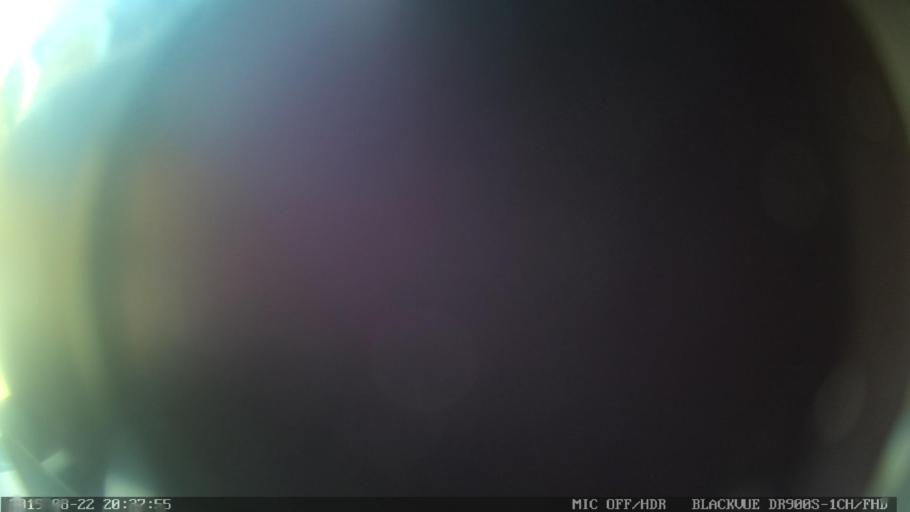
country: PT
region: Portalegre
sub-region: Nisa
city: Nisa
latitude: 39.6792
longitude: -7.7412
